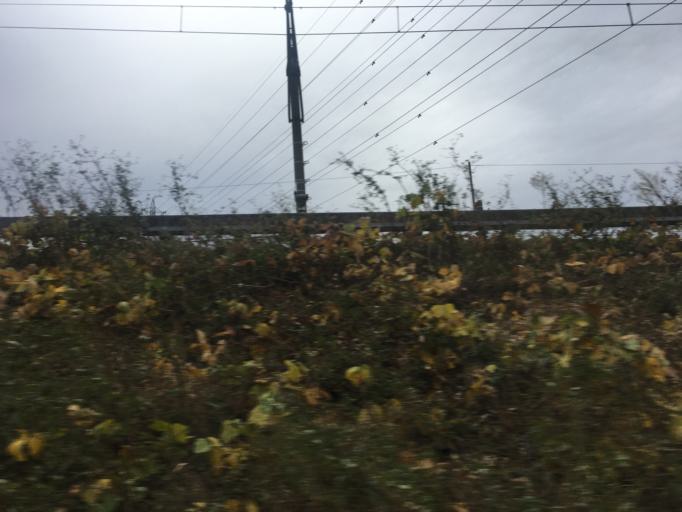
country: JP
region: Chiba
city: Nagareyama
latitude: 35.8312
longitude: 139.9106
